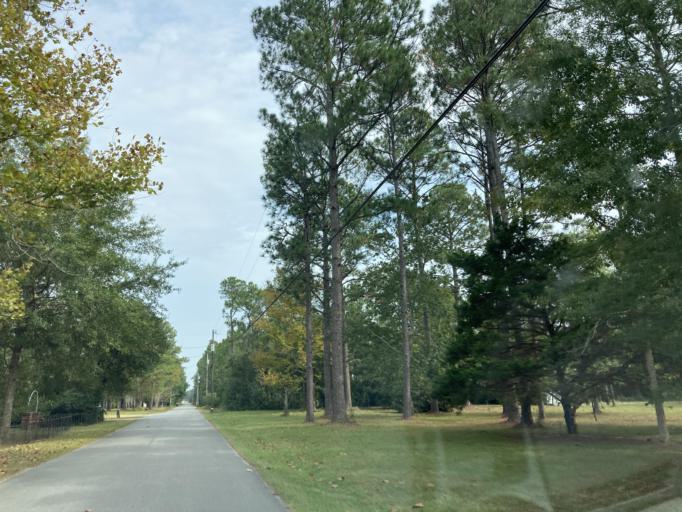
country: US
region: Mississippi
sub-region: Jackson County
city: Saint Martin
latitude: 30.4703
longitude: -88.8556
